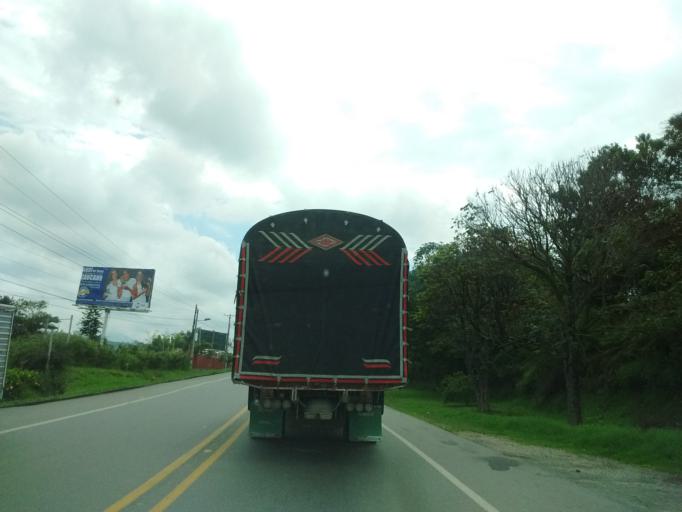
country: CO
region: Cauca
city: Cajibio
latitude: 2.5263
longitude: -76.5525
